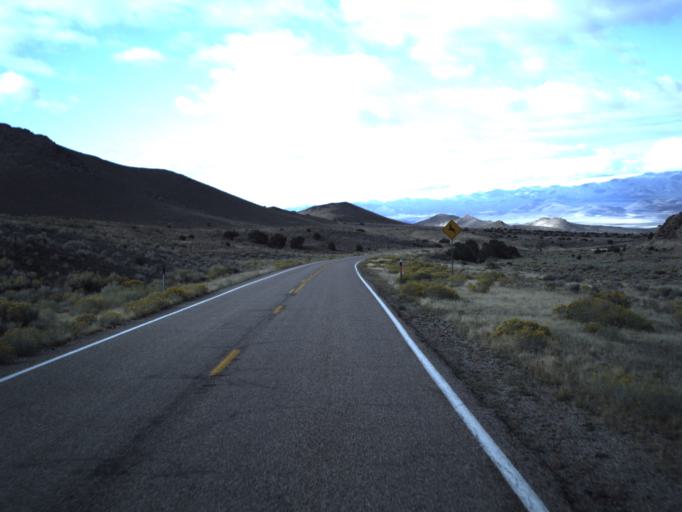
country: US
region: Utah
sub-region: Beaver County
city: Milford
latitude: 38.4374
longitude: -113.2731
